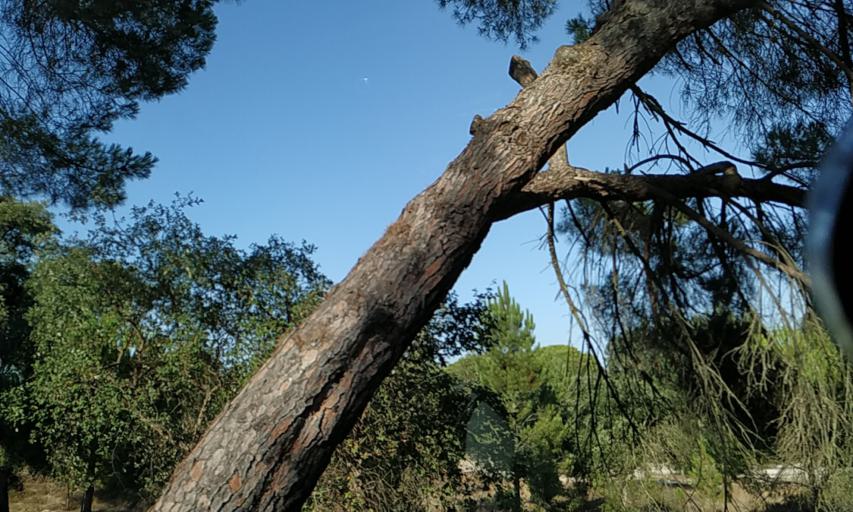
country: PT
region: Santarem
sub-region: Coruche
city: Coruche
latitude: 38.9727
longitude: -8.5385
